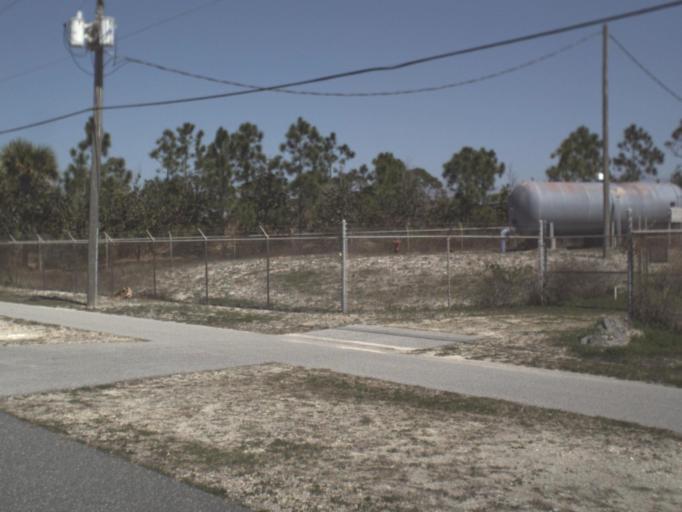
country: US
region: Florida
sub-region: Gulf County
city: Port Saint Joe
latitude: 29.7334
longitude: -85.3919
